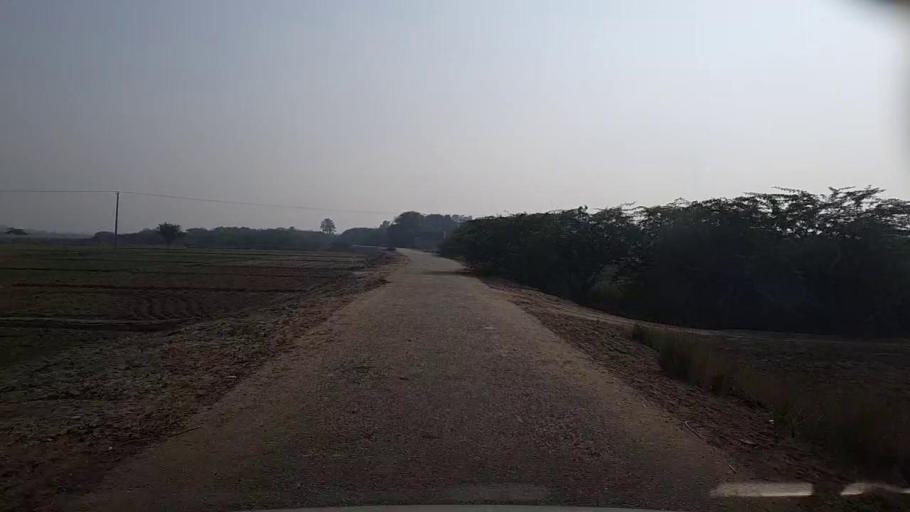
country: PK
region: Sindh
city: Kandiari
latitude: 27.0512
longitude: 68.4616
